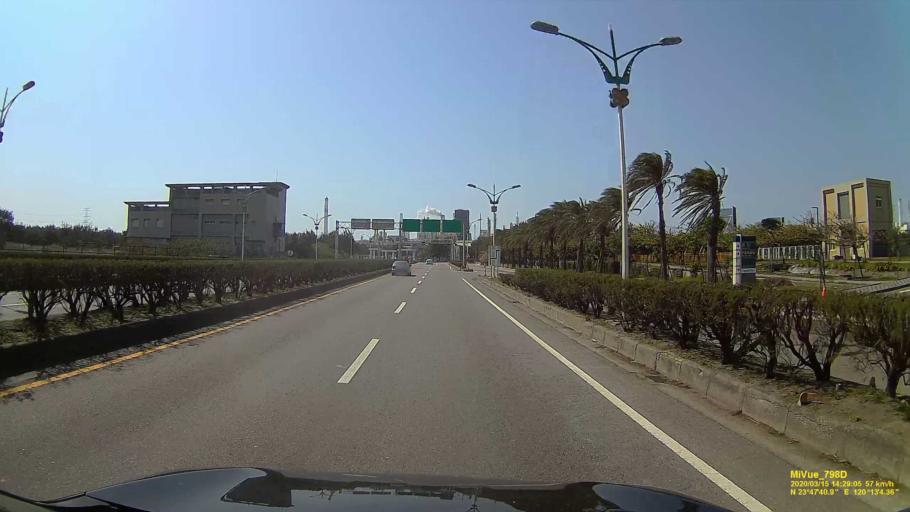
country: TW
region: Taiwan
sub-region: Yunlin
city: Douliu
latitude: 23.7948
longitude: 120.2175
